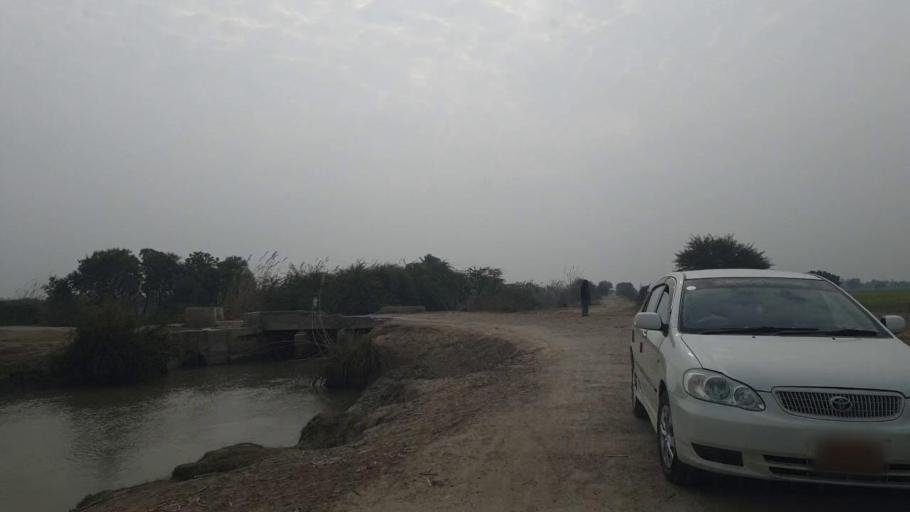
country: PK
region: Sindh
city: Tando Adam
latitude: 25.7245
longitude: 68.7264
